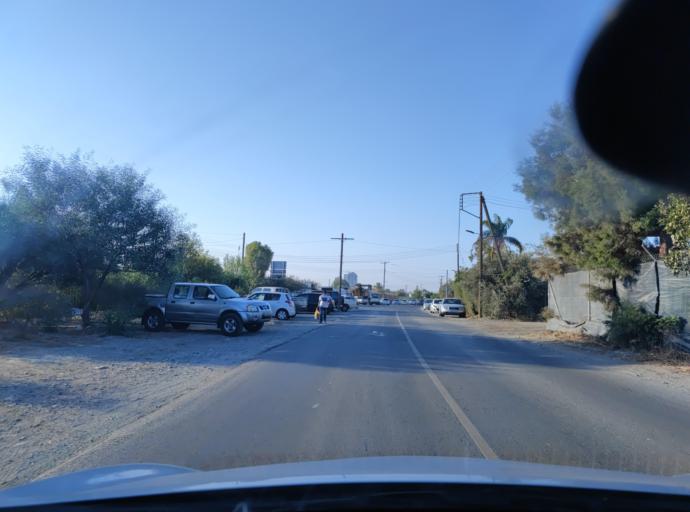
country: CY
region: Limassol
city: Mouttagiaka
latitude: 34.7175
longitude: 33.0891
